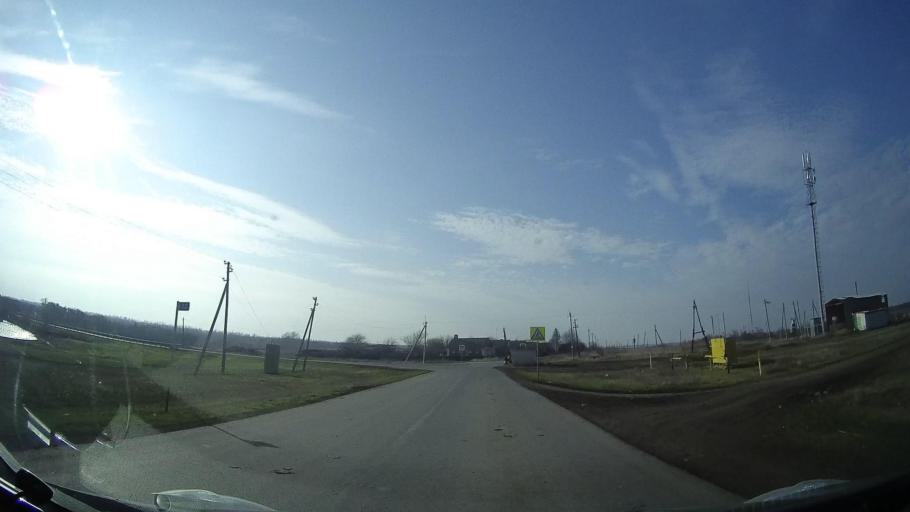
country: RU
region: Rostov
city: Mechetinskaya
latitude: 46.9137
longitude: 40.5363
